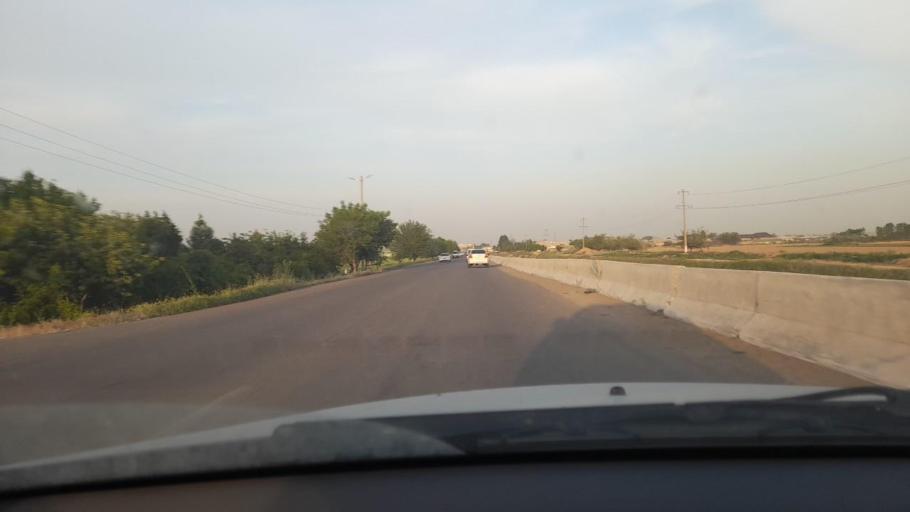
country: UZ
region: Sirdaryo
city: Guliston
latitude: 40.5076
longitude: 68.7396
